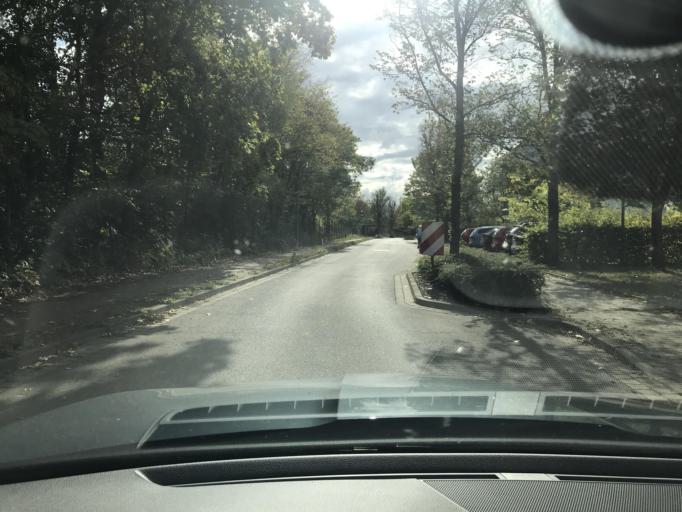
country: DE
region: Saxony-Anhalt
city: Quedlinburg
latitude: 51.7766
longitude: 11.1469
